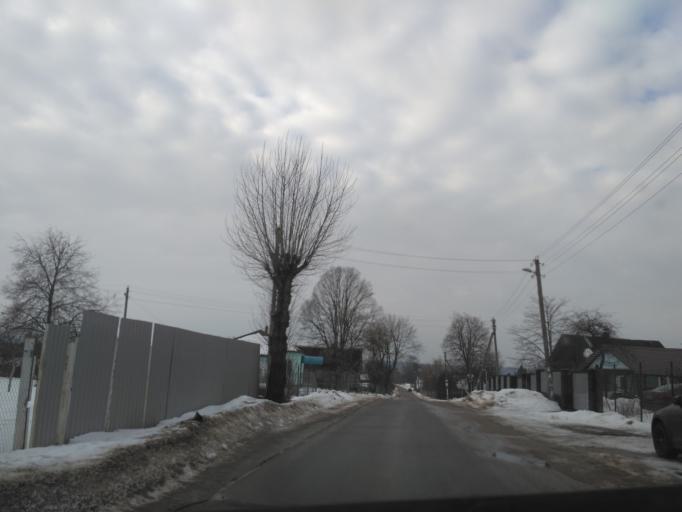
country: BY
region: Minsk
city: Zamostochcha
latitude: 53.8909
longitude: 27.9201
